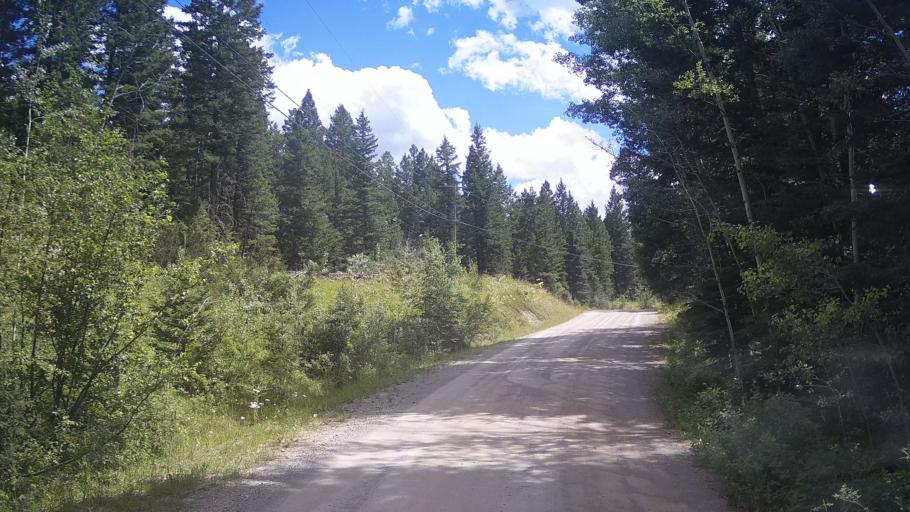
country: CA
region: British Columbia
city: Lillooet
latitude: 51.2865
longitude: -121.9690
